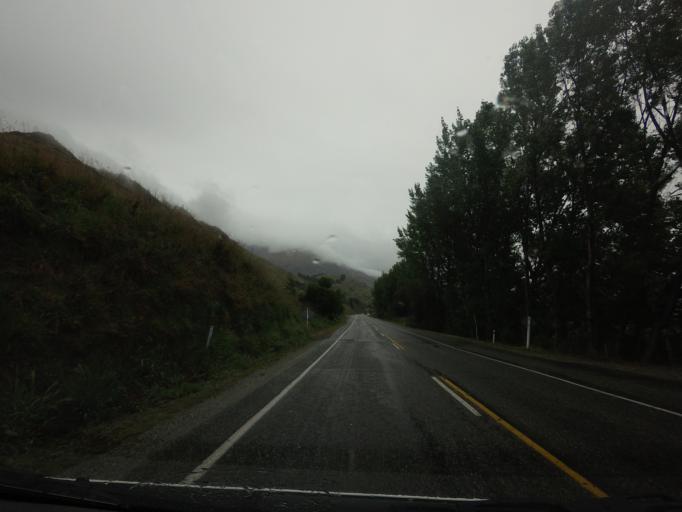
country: NZ
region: Otago
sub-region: Queenstown-Lakes District
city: Arrowtown
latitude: -44.9813
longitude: 168.8231
